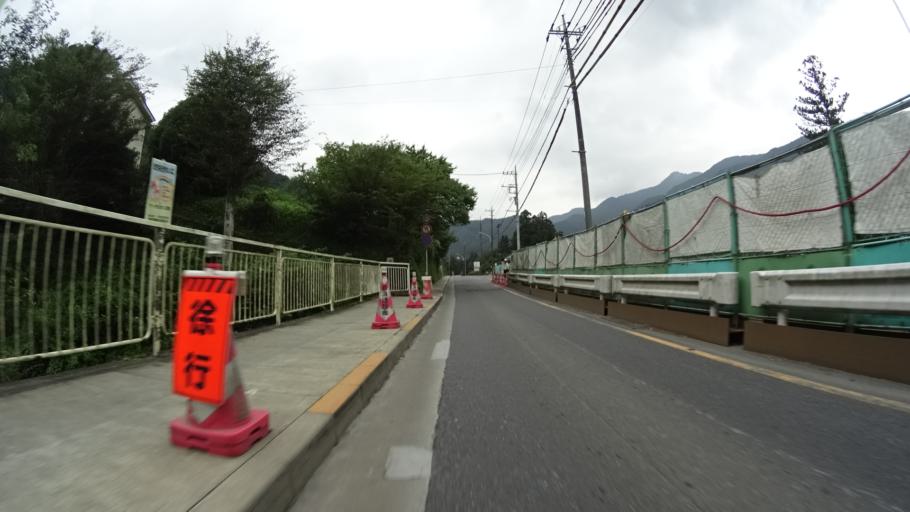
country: JP
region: Tokyo
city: Ome
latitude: 35.8028
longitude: 139.1942
